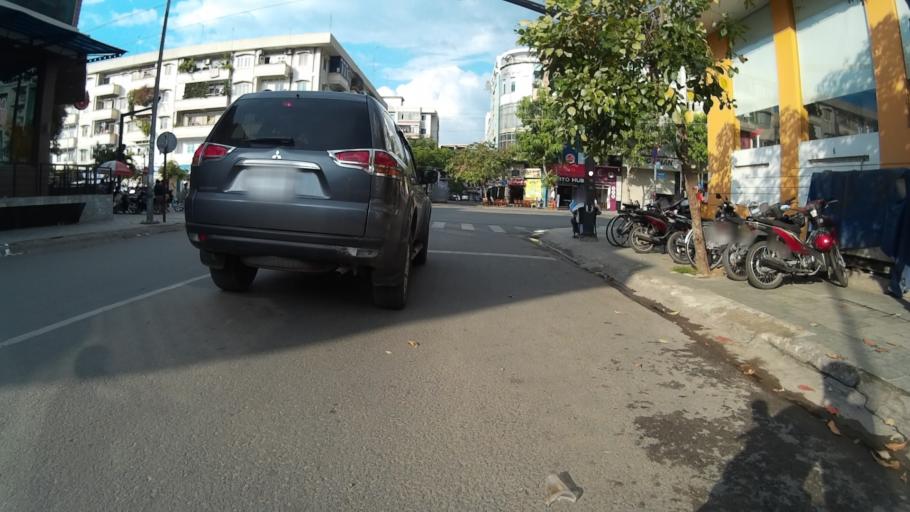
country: VN
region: Ho Chi Minh City
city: Quan Binh Thanh
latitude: 10.7983
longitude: 106.6875
